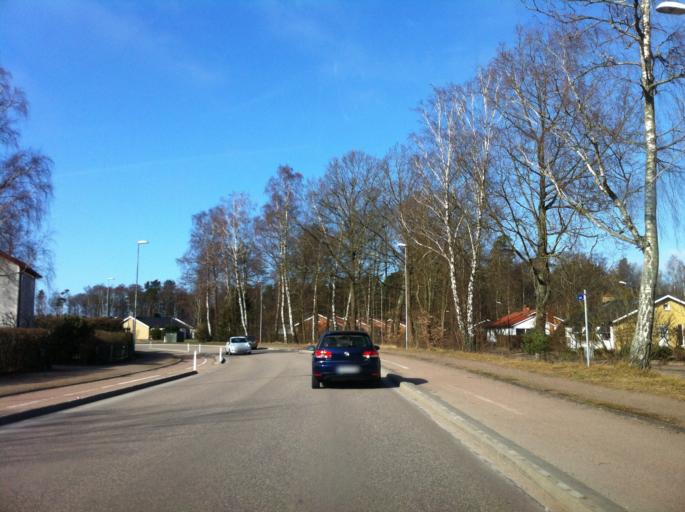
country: SE
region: Skane
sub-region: Angelholms Kommun
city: AEngelholm
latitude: 56.2526
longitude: 12.8555
